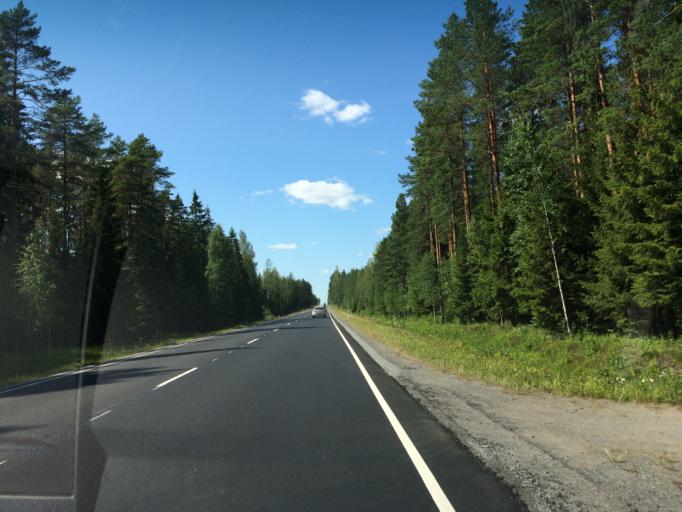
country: FI
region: Pirkanmaa
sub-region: Lounais-Pirkanmaa
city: Kiikoinen
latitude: 61.4738
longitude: 22.4960
